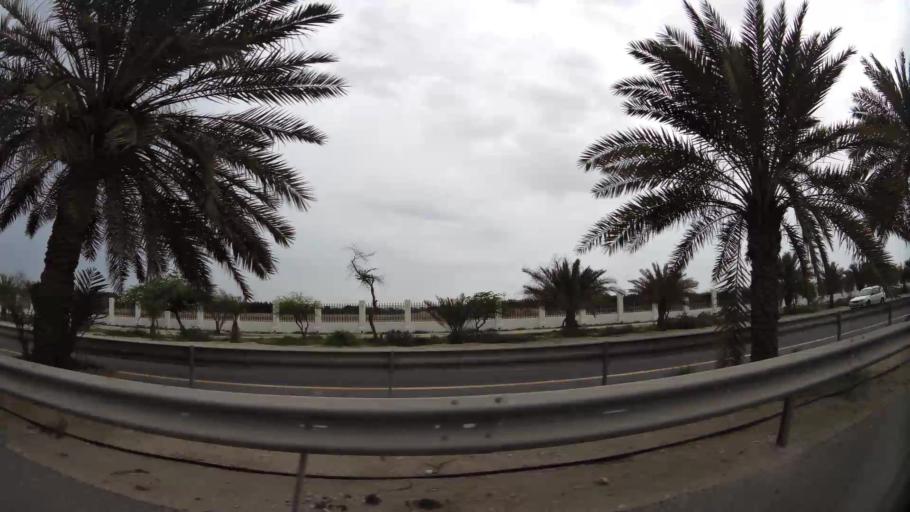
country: BH
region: Central Governorate
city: Dar Kulayb
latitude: 26.0667
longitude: 50.5230
